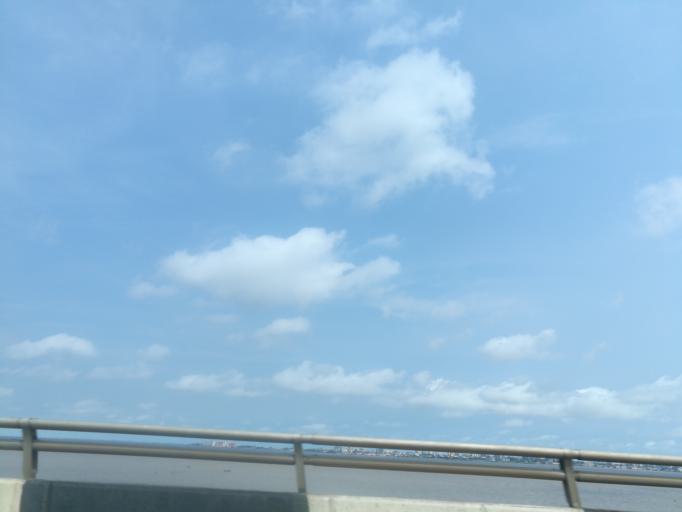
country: NG
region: Lagos
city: Ebute Metta
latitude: 6.4863
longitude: 3.3954
